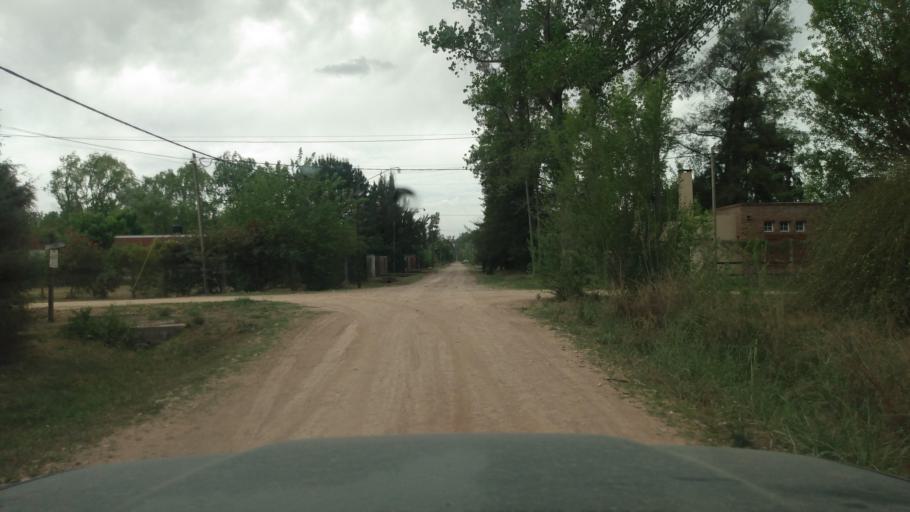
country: AR
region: Buenos Aires
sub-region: Partido de Lujan
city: Lujan
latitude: -34.5913
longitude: -59.1369
